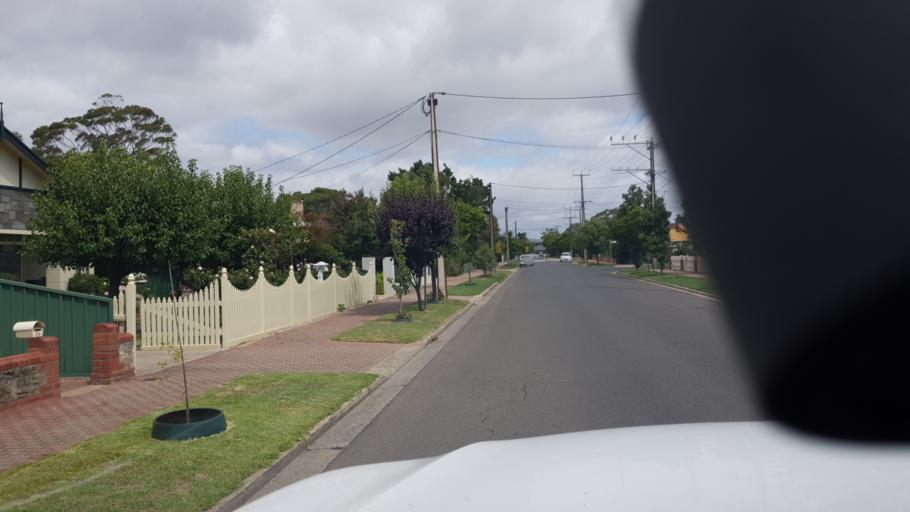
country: AU
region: South Australia
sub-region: Holdfast Bay
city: Glenelg East
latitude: -34.9819
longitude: 138.5287
